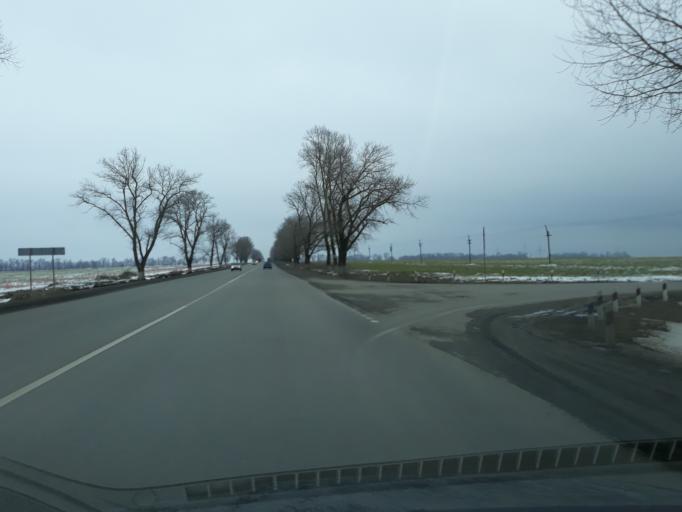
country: RU
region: Rostov
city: Primorka
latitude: 47.3075
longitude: 39.1374
